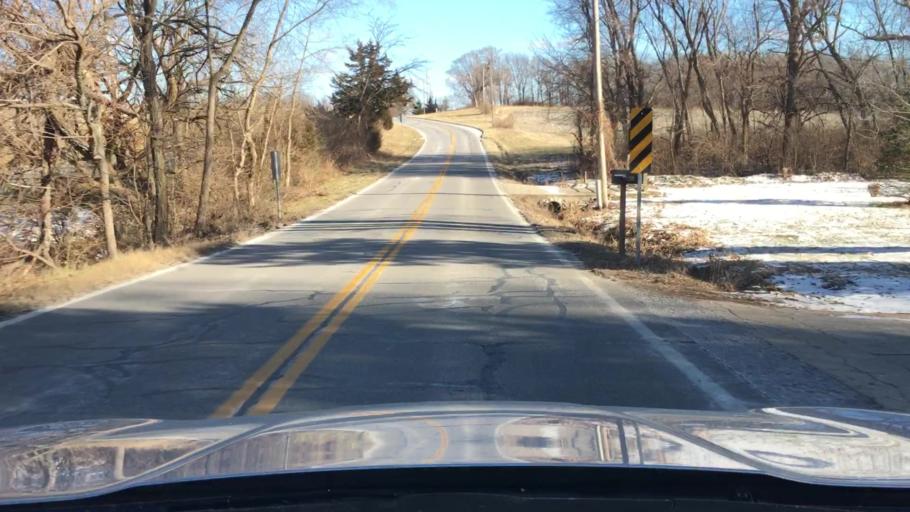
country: US
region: Missouri
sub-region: Jackson County
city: Lees Summit
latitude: 38.8896
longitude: -94.4004
